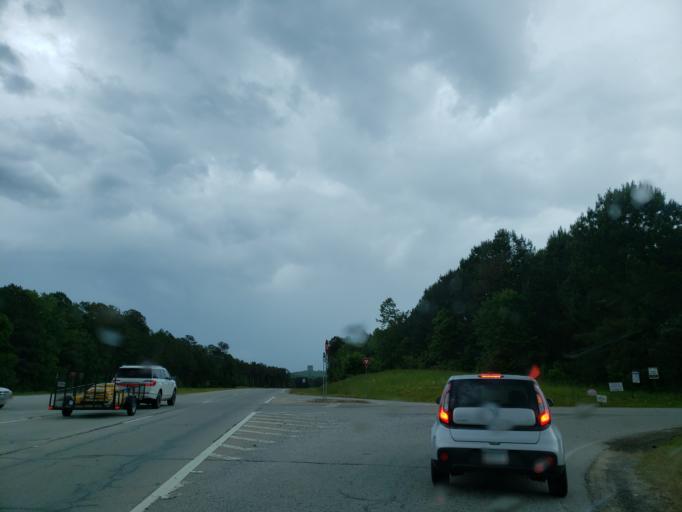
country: US
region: Georgia
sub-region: Haralson County
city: Buchanan
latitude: 33.8159
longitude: -85.1925
